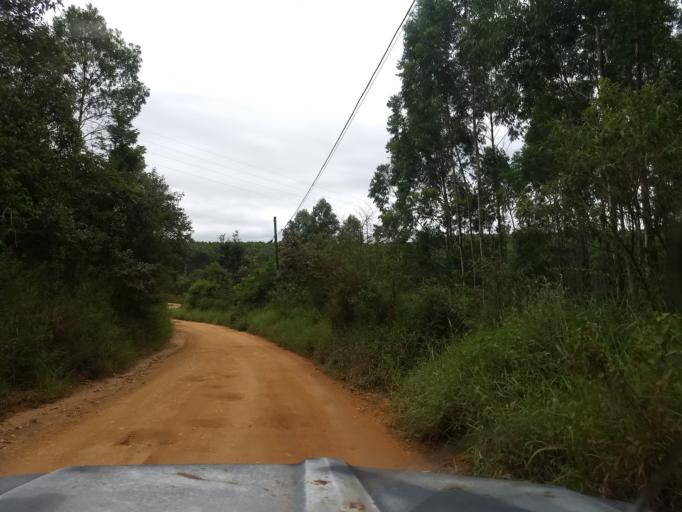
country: BR
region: Sao Paulo
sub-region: Cabreuva
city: Cabreuva
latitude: -23.3932
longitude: -47.1949
